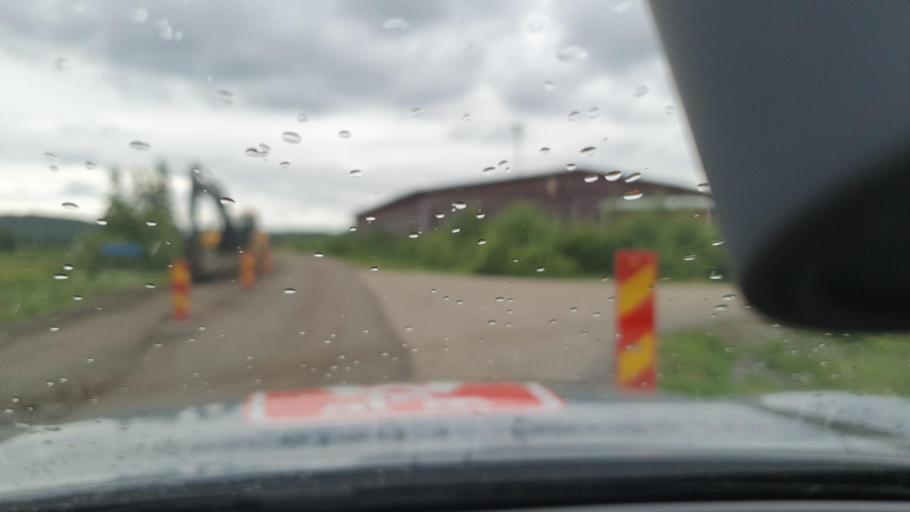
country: SE
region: Norrbotten
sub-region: Overtornea Kommun
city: OEvertornea
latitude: 66.4001
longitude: 23.6136
